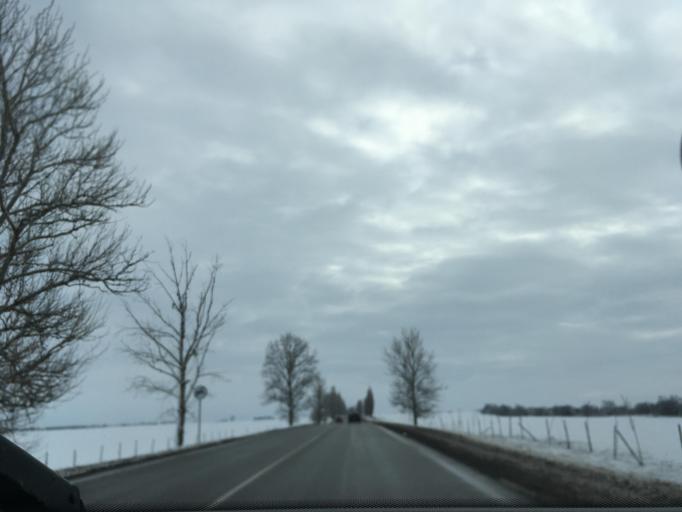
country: UA
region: Luhansk
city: Lozno-Oleksandrivka
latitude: 49.9632
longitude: 38.9398
